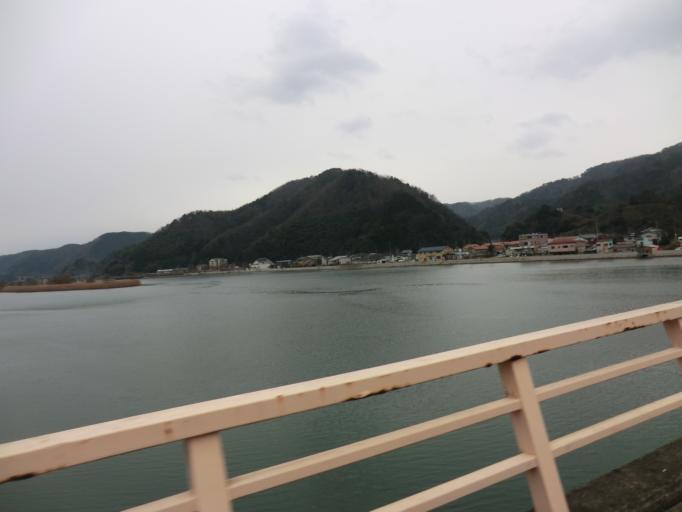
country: JP
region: Hyogo
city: Toyooka
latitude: 35.6073
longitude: 134.8058
